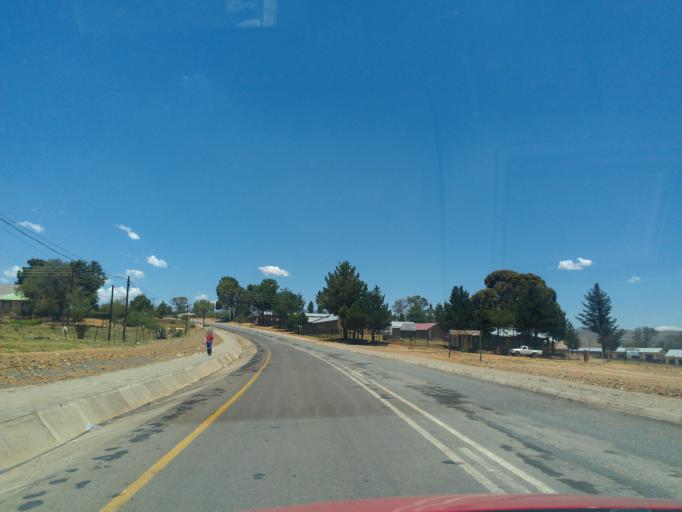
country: LS
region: Berea
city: Teyateyaneng
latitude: -29.1125
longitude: 27.9674
